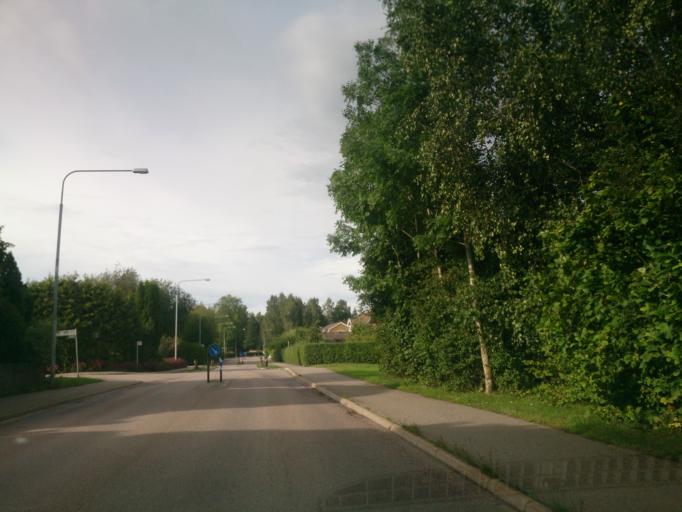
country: SE
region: OEstergoetland
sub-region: Linkopings Kommun
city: Malmslatt
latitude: 58.4201
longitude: 15.5010
